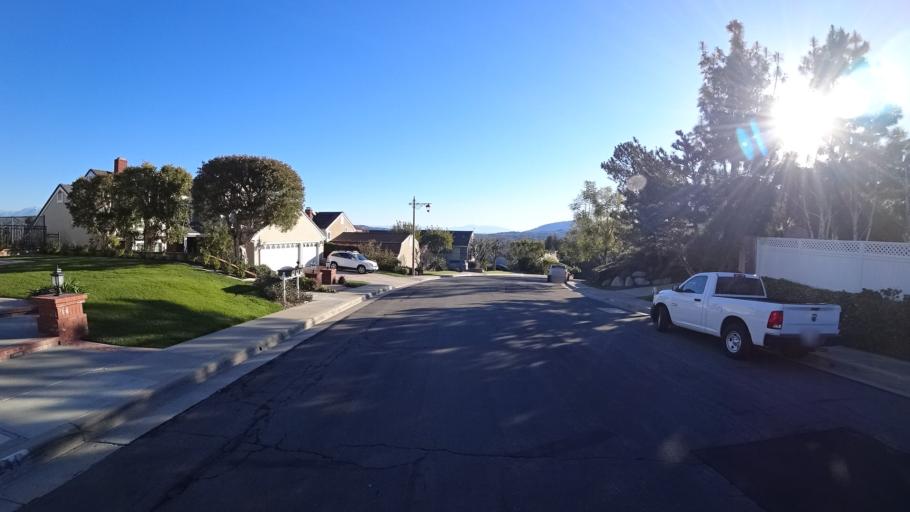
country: US
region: California
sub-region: Orange County
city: Villa Park
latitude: 33.8392
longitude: -117.8030
